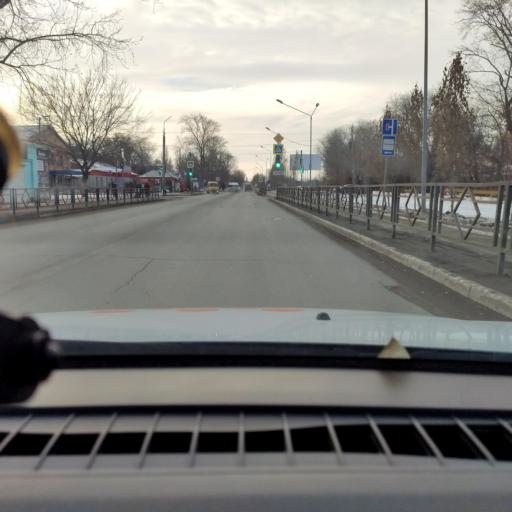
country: RU
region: Samara
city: Chapayevsk
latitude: 52.9776
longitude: 49.7058
